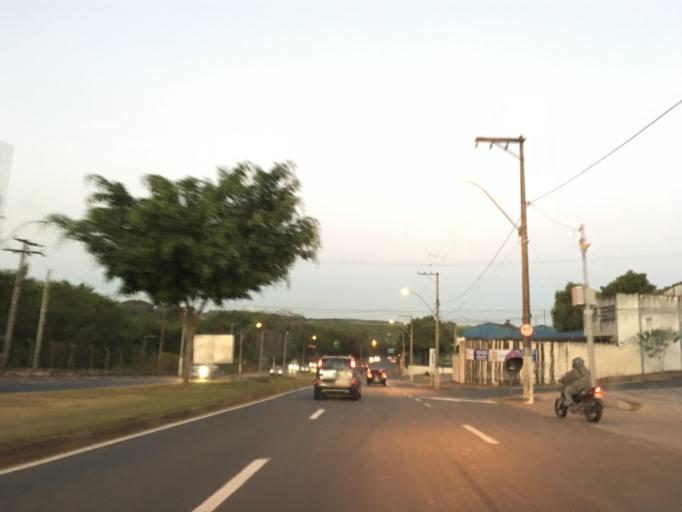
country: BR
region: Sao Paulo
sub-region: Piracicaba
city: Piracicaba
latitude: -22.7160
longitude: -47.6280
